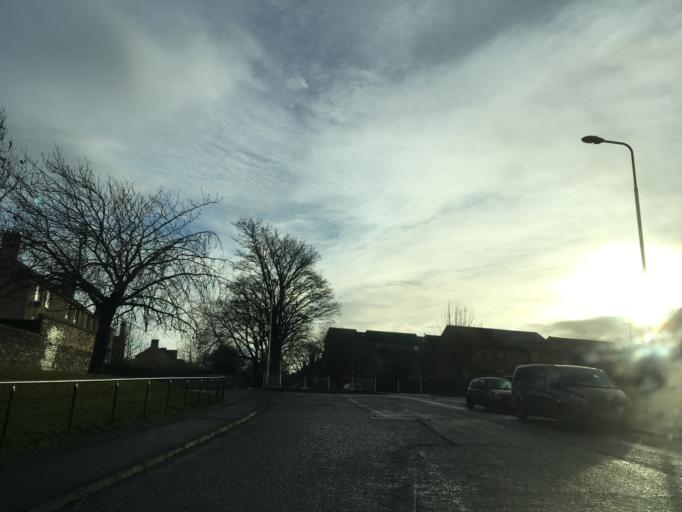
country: GB
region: Scotland
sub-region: Edinburgh
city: Colinton
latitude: 55.9326
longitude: -3.2442
